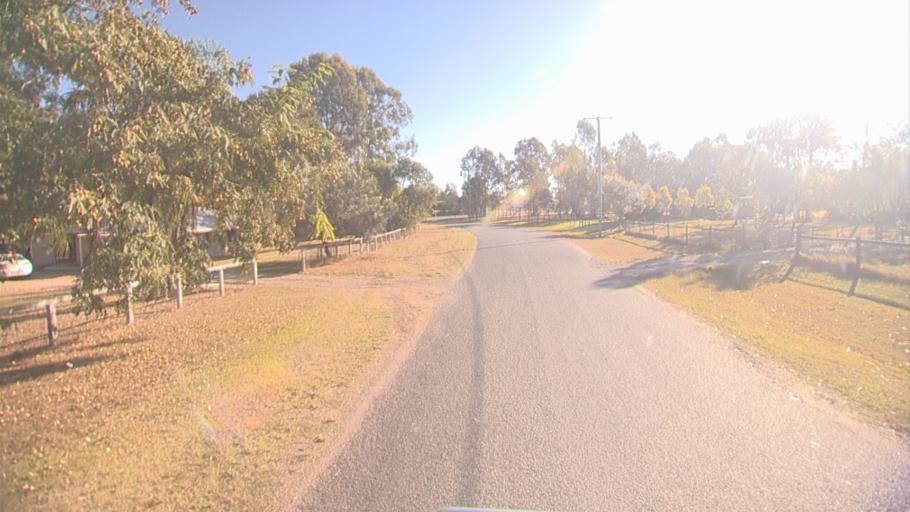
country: AU
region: Queensland
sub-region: Logan
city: Cedar Vale
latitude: -27.8286
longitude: 153.0218
